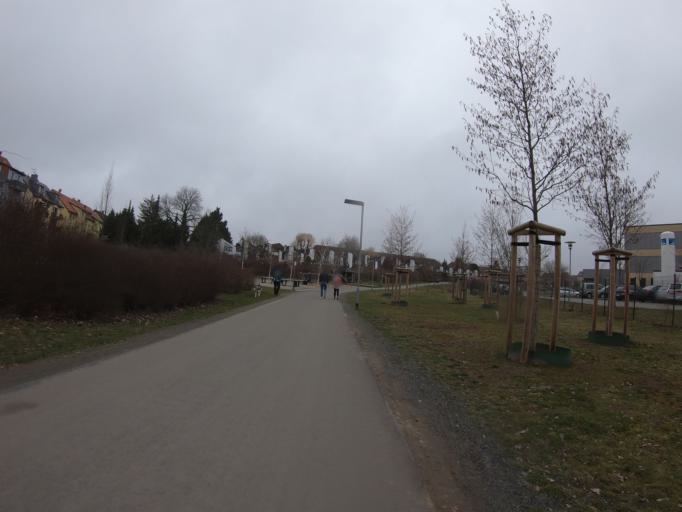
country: DE
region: Lower Saxony
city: Braunschweig
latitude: 52.2747
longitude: 10.5010
